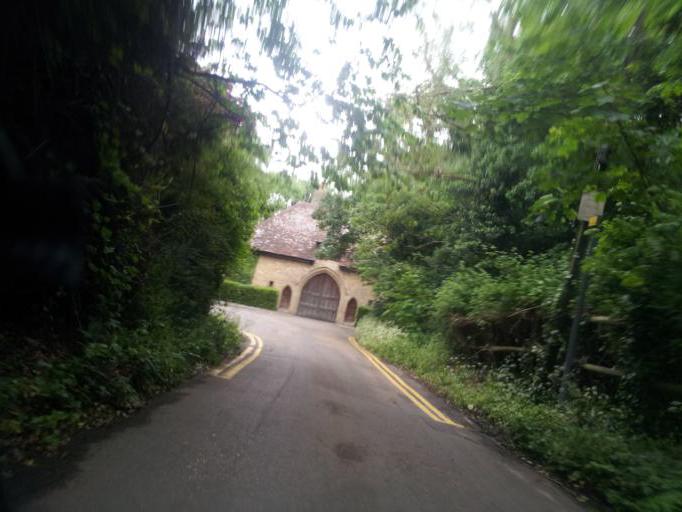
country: GB
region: England
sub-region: Kent
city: Maidstone
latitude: 51.2921
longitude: 0.5060
